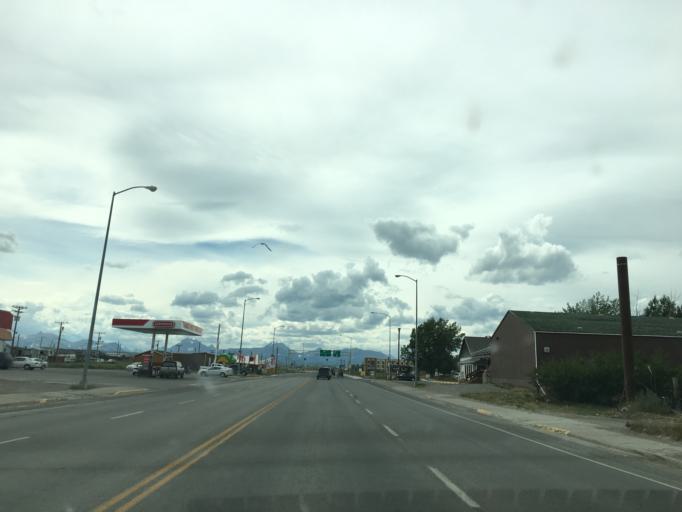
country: US
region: Montana
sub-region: Glacier County
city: Browning
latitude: 48.5560
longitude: -113.0191
